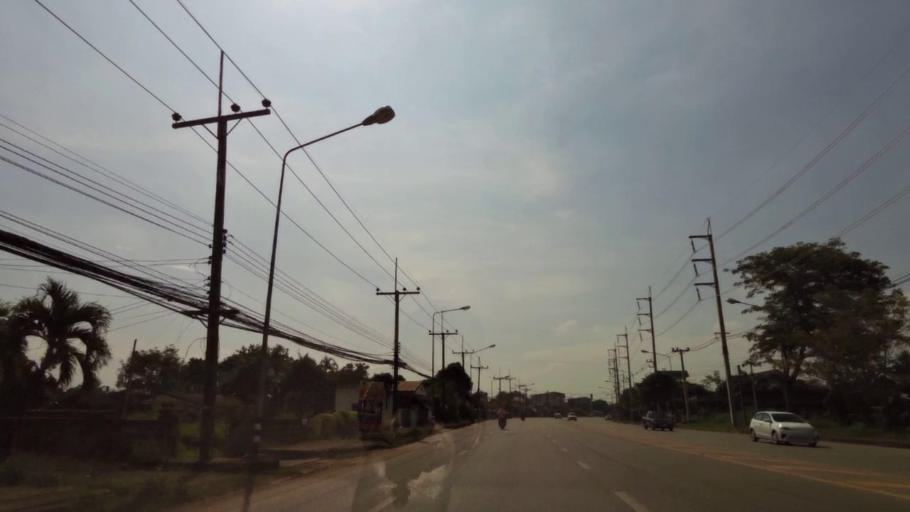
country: TH
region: Chiang Rai
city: Chiang Rai
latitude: 19.8855
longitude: 99.8003
